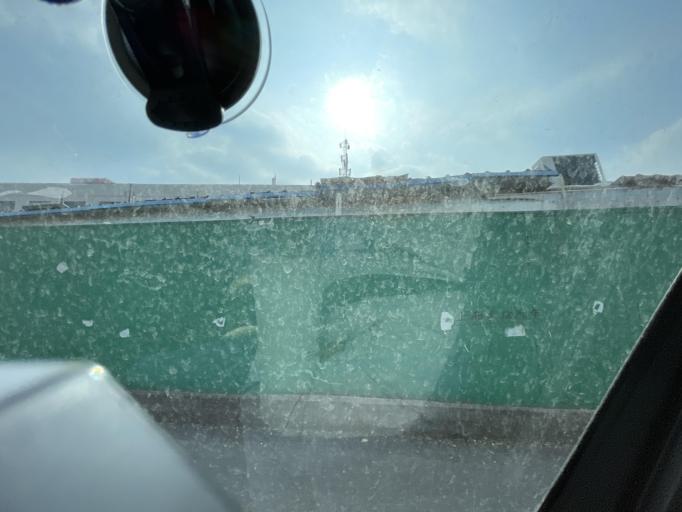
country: CN
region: Shanghai Shi
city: Yangpu
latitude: 31.3169
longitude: 121.5184
